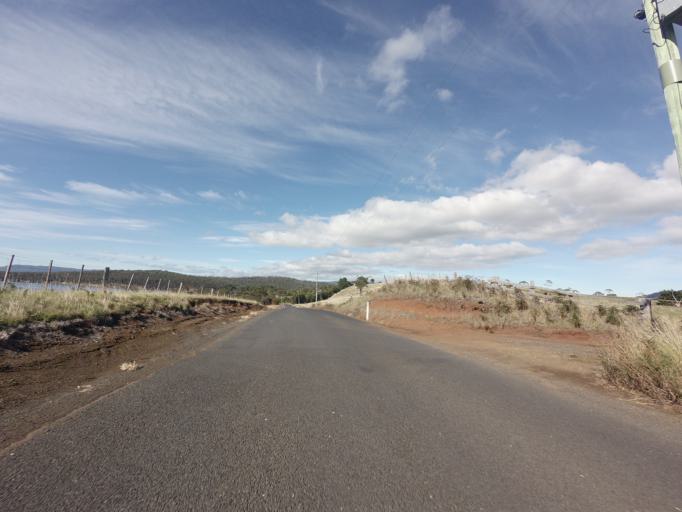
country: AU
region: Tasmania
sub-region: Clarence
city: Sandford
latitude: -43.0151
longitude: 147.7191
